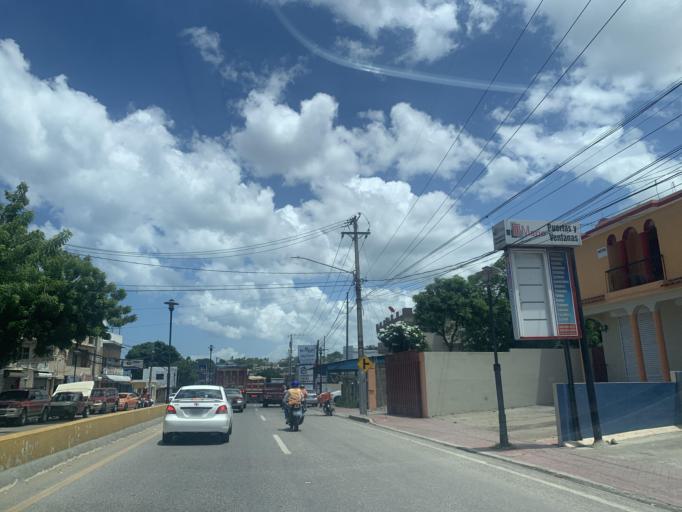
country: DO
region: Puerto Plata
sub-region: Puerto Plata
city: Puerto Plata
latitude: 19.7912
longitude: -70.7029
